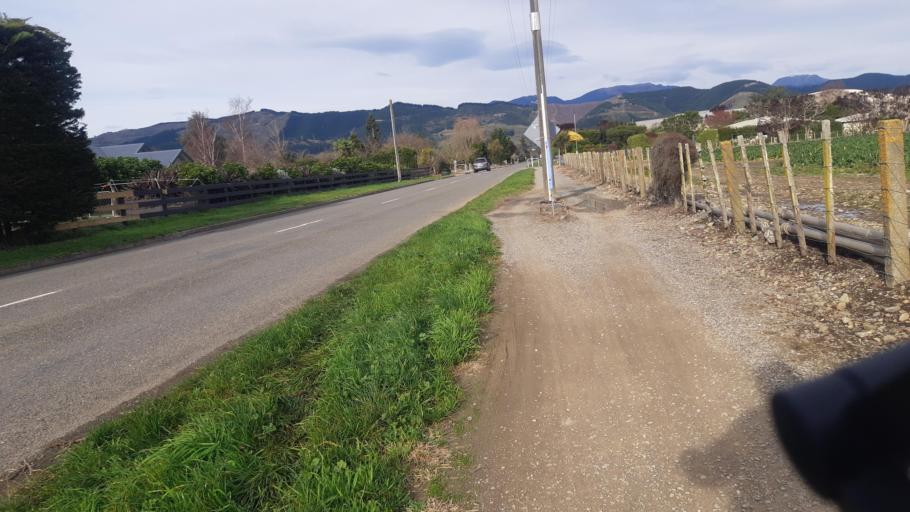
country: NZ
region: Tasman
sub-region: Tasman District
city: Richmond
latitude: -41.3451
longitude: 173.1433
